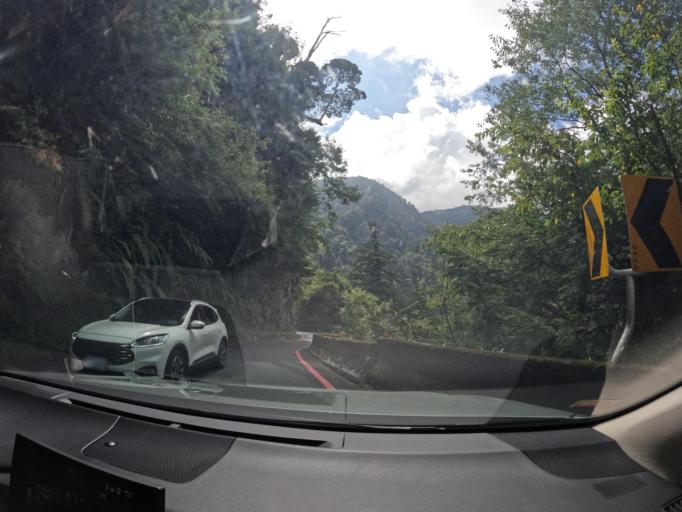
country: TW
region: Taiwan
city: Yujing
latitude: 23.2628
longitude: 120.9214
